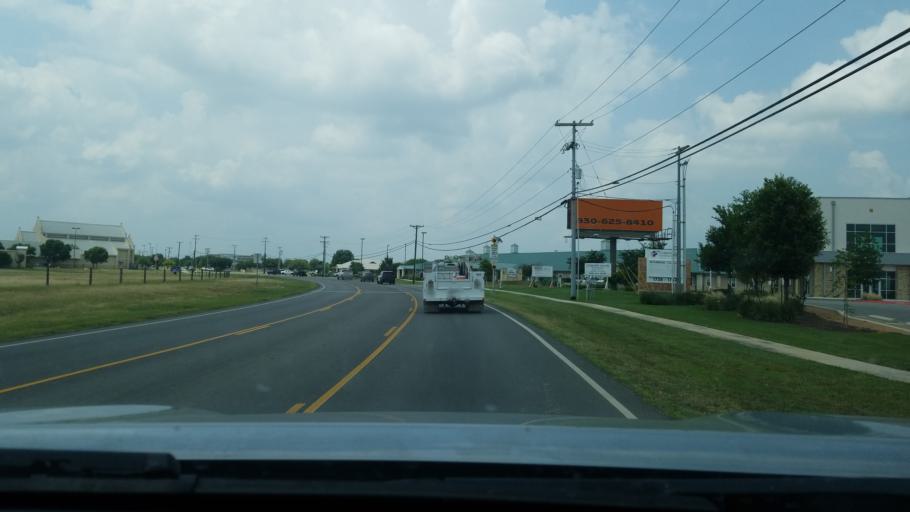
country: US
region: Texas
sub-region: Comal County
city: New Braunfels
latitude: 29.7272
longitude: -98.0950
